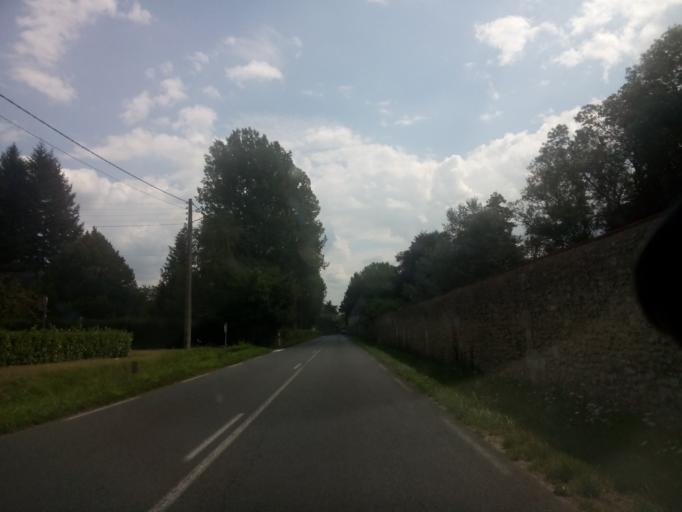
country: FR
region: Centre
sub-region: Departement d'Indre-et-Loire
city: Cheille
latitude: 47.2689
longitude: 0.4335
